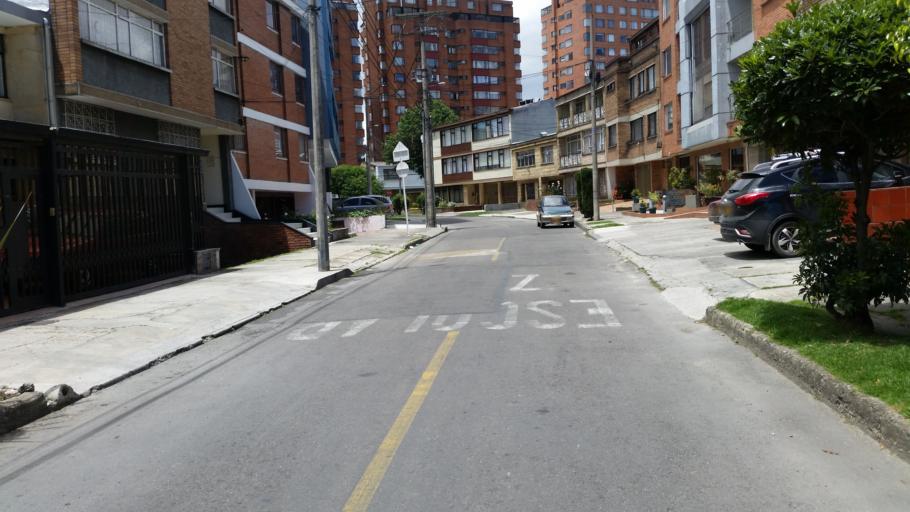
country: CO
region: Bogota D.C.
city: Bogota
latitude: 4.6325
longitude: -74.0891
